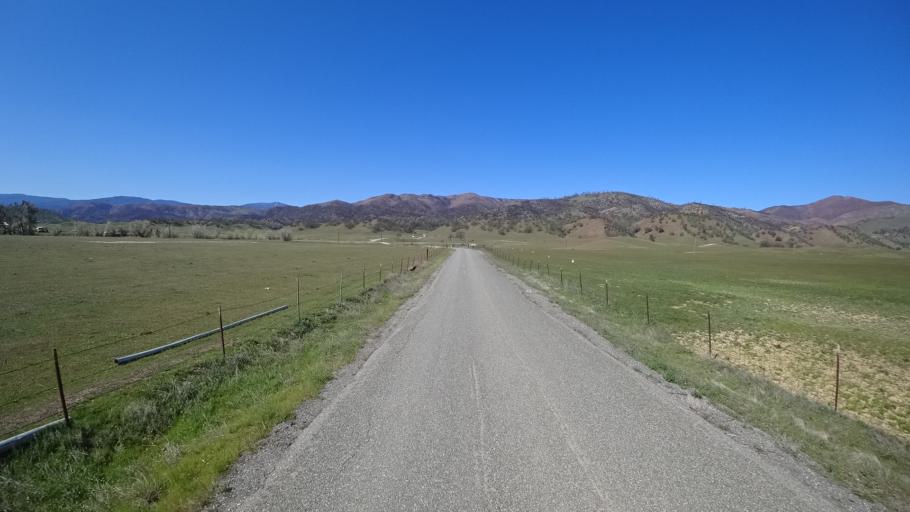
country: US
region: California
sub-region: Tehama County
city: Rancho Tehama Reserve
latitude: 39.6993
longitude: -122.5609
